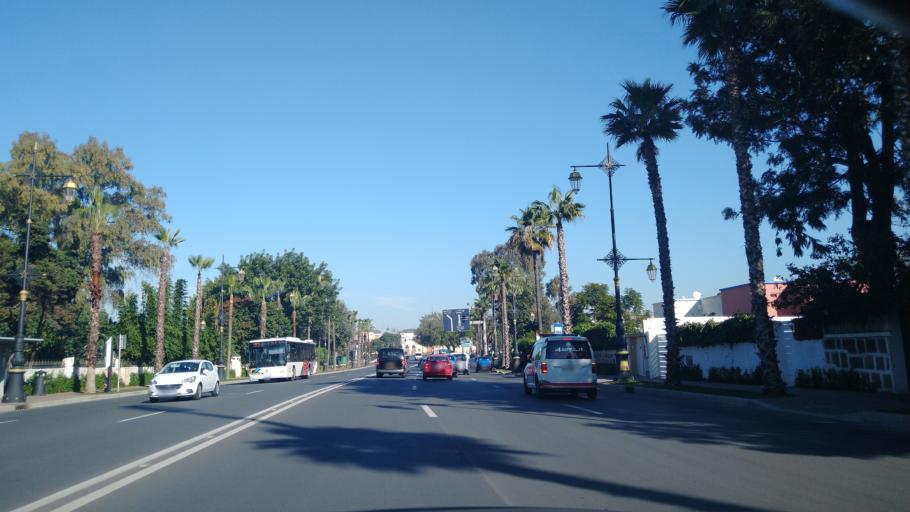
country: MA
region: Rabat-Sale-Zemmour-Zaer
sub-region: Rabat
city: Rabat
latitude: 34.0033
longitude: -6.8271
